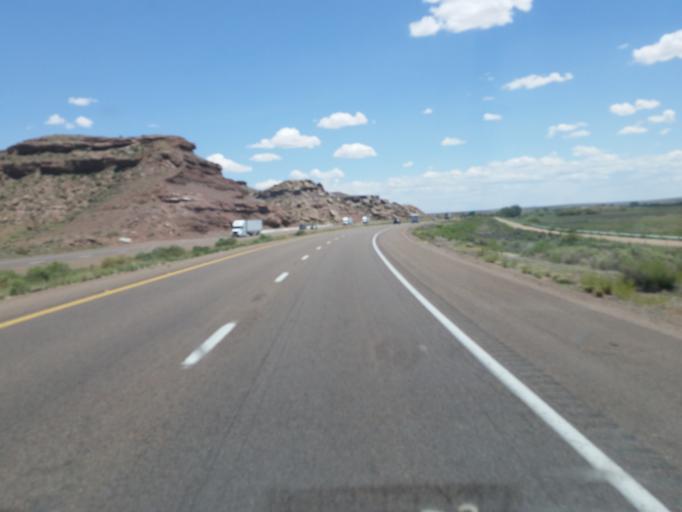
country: US
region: Arizona
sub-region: Navajo County
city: Joseph City
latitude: 34.9392
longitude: -110.2801
